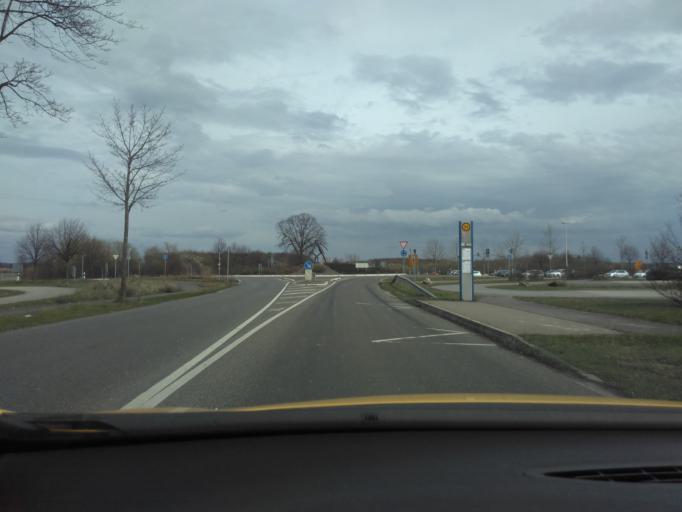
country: DE
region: North Rhine-Westphalia
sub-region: Regierungsbezirk Koln
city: Erftstadt
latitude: 50.8028
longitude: 6.7860
